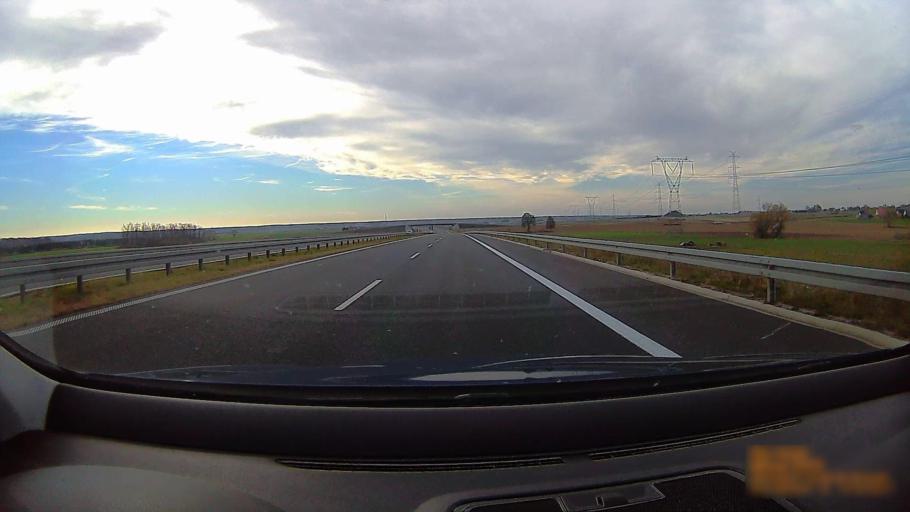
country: PL
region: Greater Poland Voivodeship
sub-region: Powiat ostrowski
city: Przygodzice
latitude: 51.6042
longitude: 17.8538
